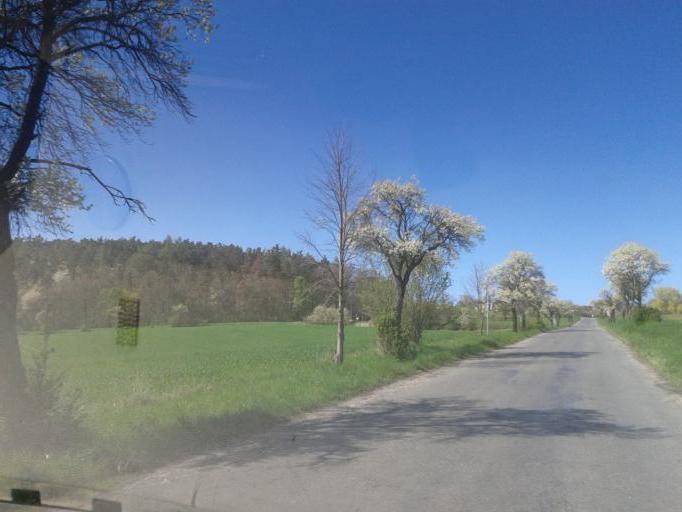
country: CZ
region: Central Bohemia
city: Revnice
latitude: 49.8893
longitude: 14.1482
